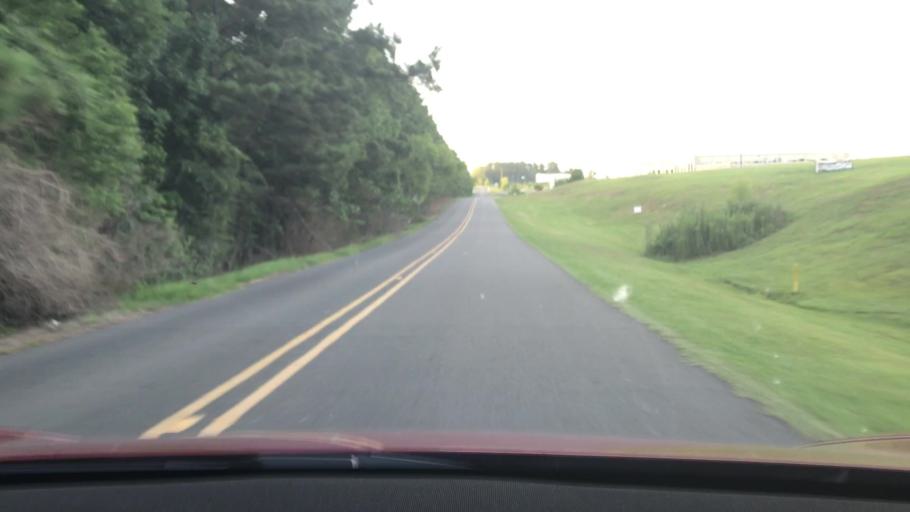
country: US
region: Louisiana
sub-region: Bossier Parish
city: Bossier City
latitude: 32.3925
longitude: -93.7547
